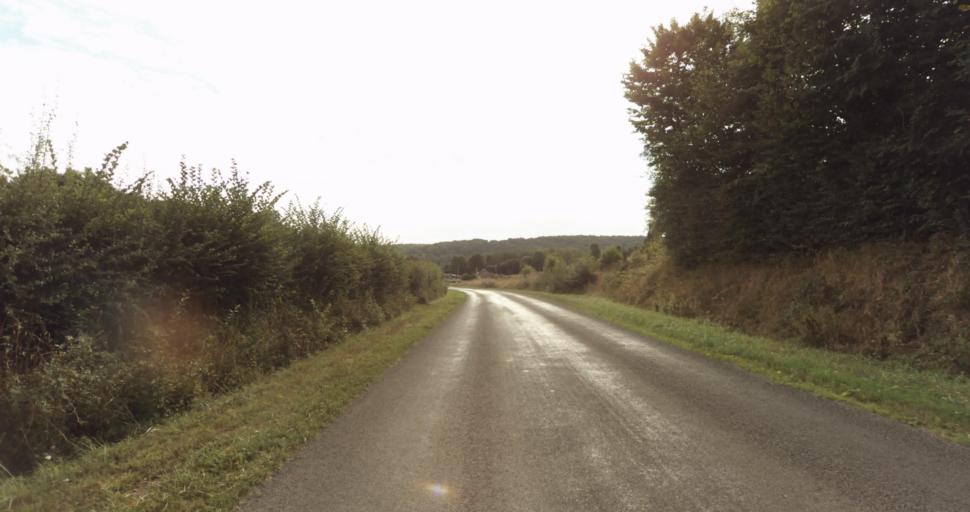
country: FR
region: Lower Normandy
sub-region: Departement de l'Orne
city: Vimoutiers
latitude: 48.9272
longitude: 0.2575
